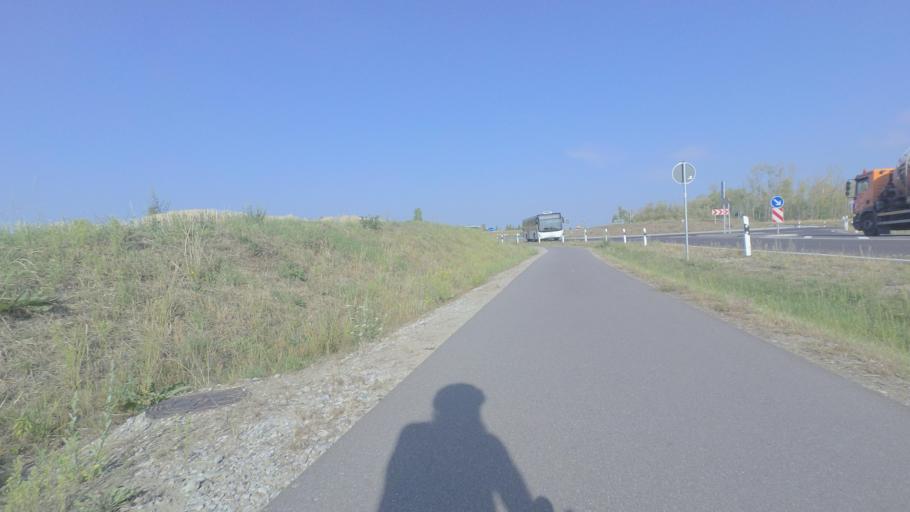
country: DE
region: Brandenburg
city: Fehrbellin
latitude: 52.8014
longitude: 12.7972
